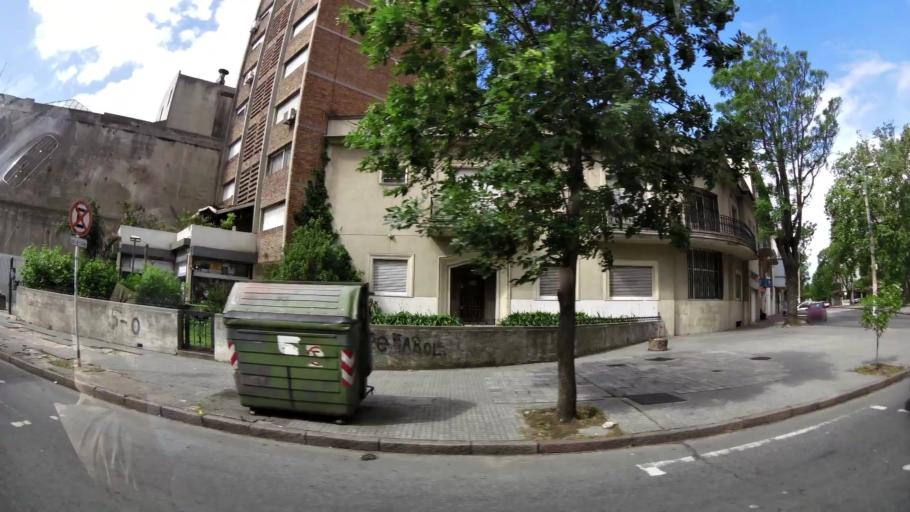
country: UY
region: Montevideo
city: Montevideo
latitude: -34.8765
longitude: -56.1978
